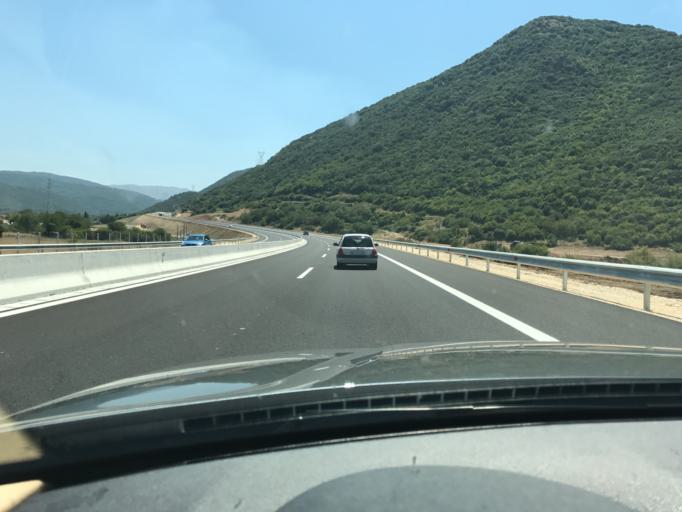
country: GR
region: Epirus
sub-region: Nomos Ioanninon
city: Agia Kyriaki
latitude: 39.5210
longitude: 20.8811
